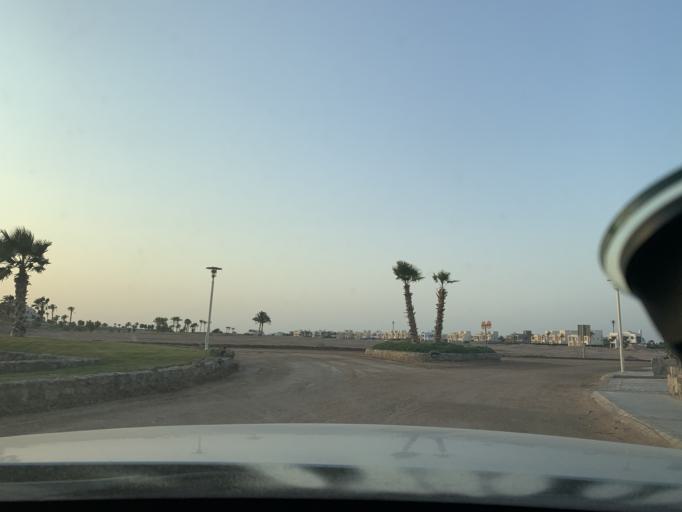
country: EG
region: Red Sea
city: El Gouna
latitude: 27.4110
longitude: 33.6662
